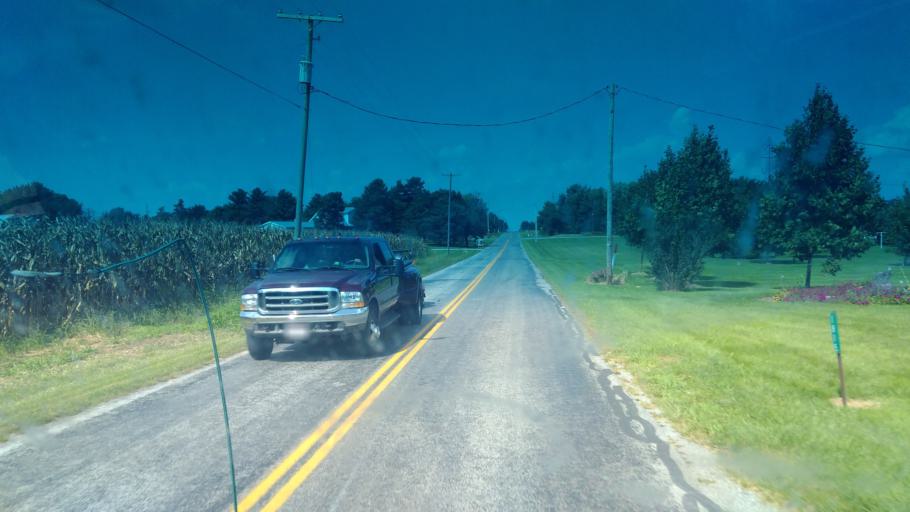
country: US
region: Ohio
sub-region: Hardin County
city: Ada
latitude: 40.7156
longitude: -83.9253
